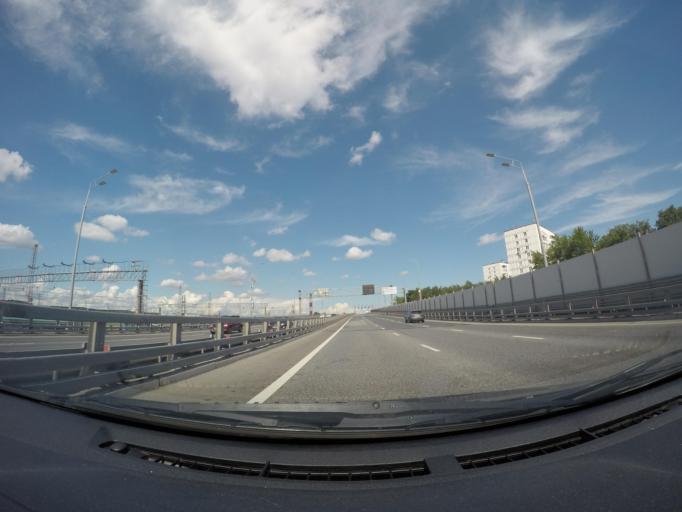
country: RU
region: Moscow
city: Ryazanskiy
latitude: 55.7421
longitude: 37.7555
